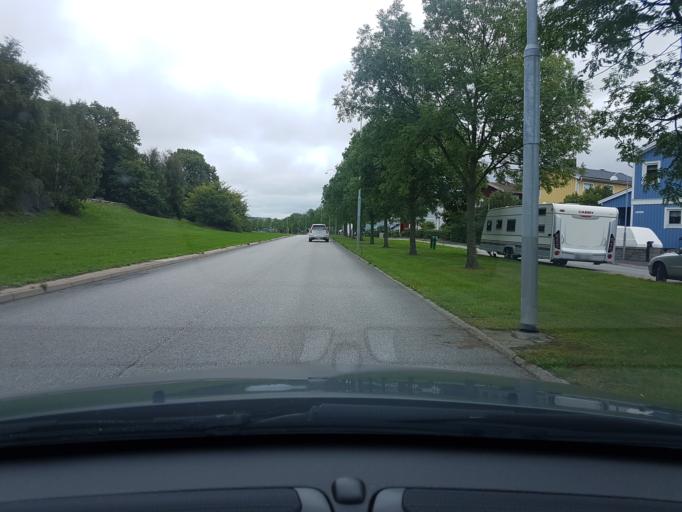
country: SE
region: Vaestra Goetaland
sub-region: Goteborg
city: Majorna
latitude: 57.7058
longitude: 11.8941
